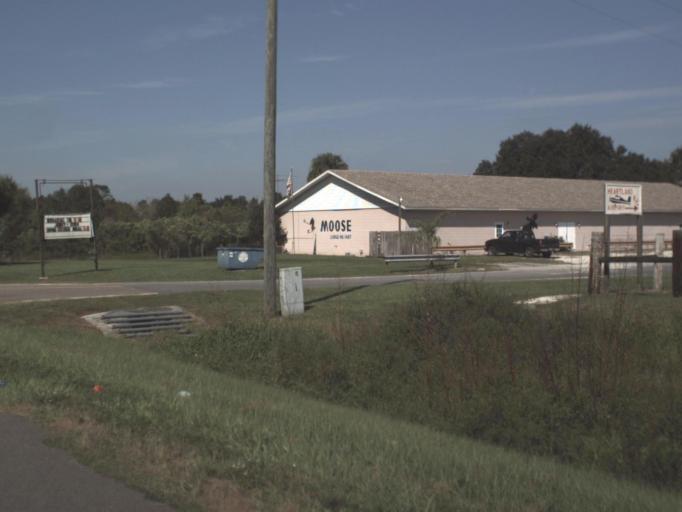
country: US
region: Florida
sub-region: Hardee County
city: Wauchula
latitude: 27.5514
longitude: -81.7836
